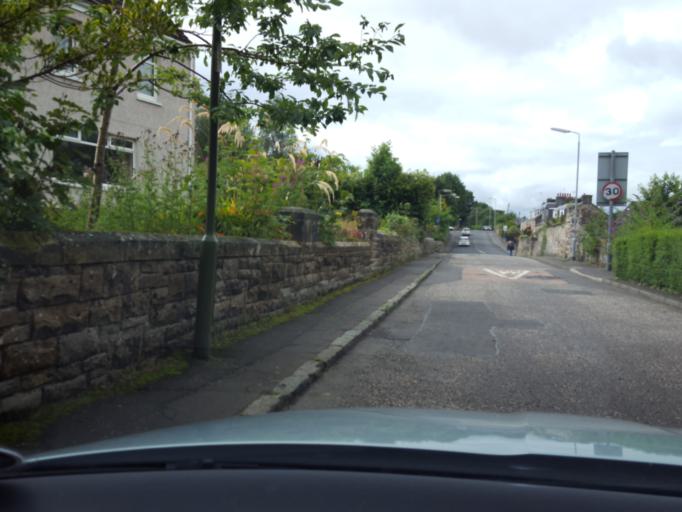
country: GB
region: Scotland
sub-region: Falkirk
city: Bo'ness
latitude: 56.0147
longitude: -3.6084
